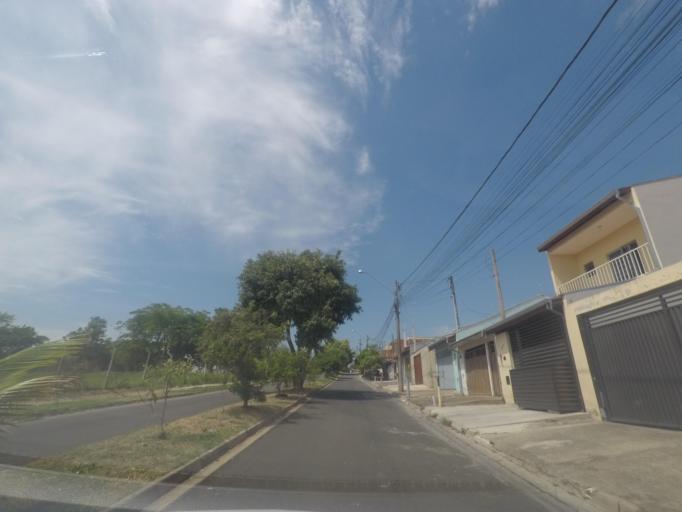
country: BR
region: Sao Paulo
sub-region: Sumare
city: Sumare
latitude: -22.7987
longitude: -47.2660
